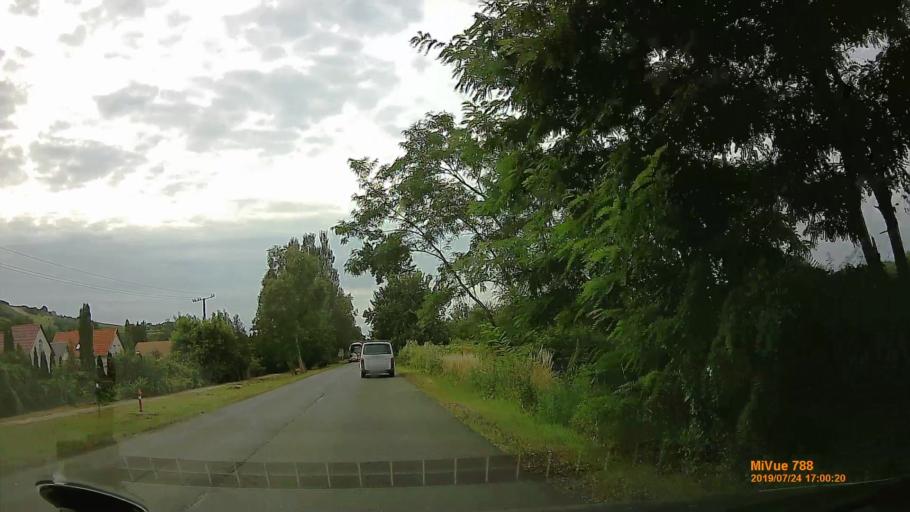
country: HU
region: Borsod-Abauj-Zemplen
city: Tokaj
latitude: 48.1441
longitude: 21.3908
